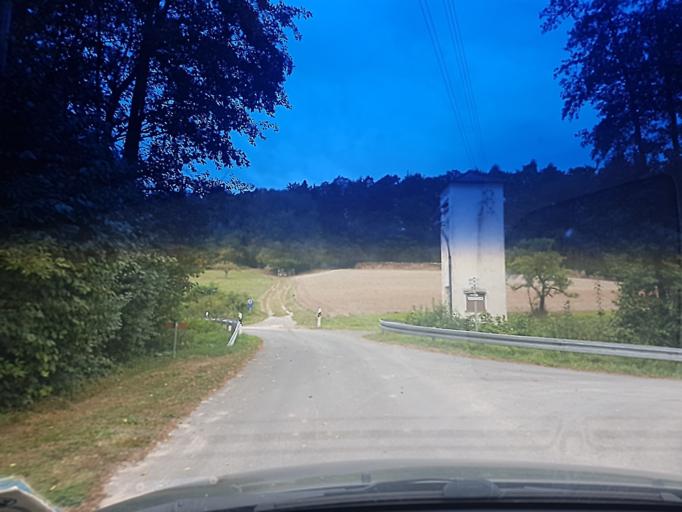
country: DE
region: Bavaria
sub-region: Regierungsbezirk Unterfranken
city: Geiselwind
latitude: 49.8147
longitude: 10.5107
